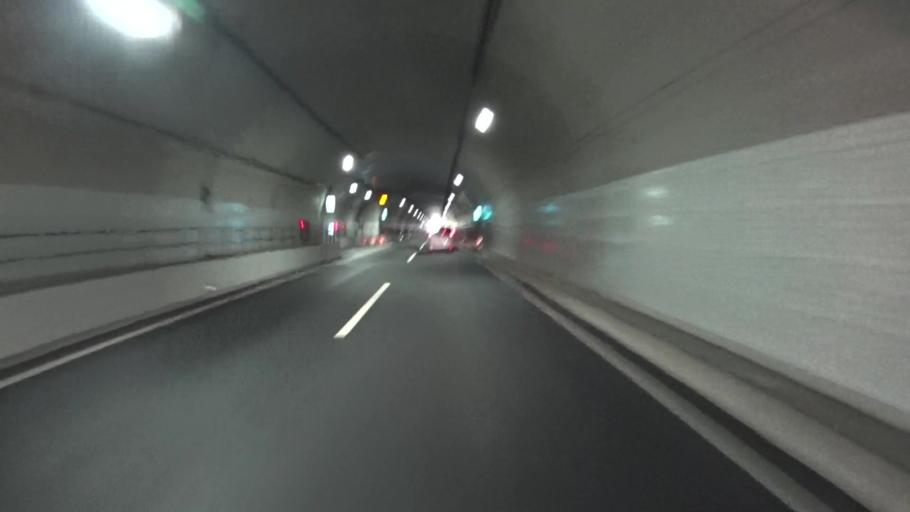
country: JP
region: Kyoto
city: Muko
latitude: 34.9395
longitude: 135.6647
